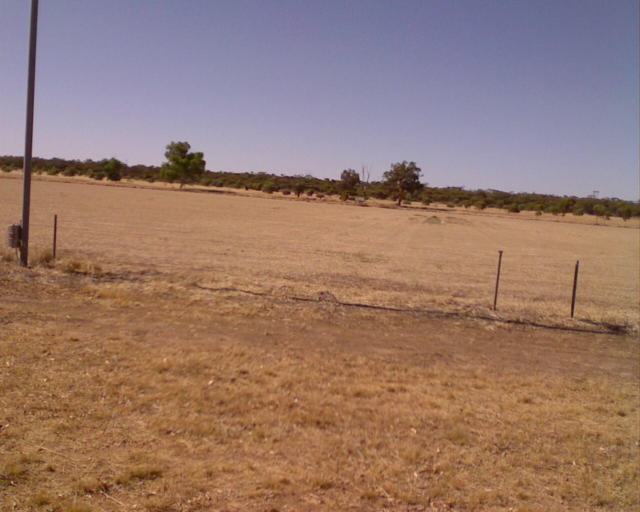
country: AU
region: Western Australia
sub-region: Wongan-Ballidu
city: Wongan Hills
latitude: -30.6060
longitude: 116.7707
